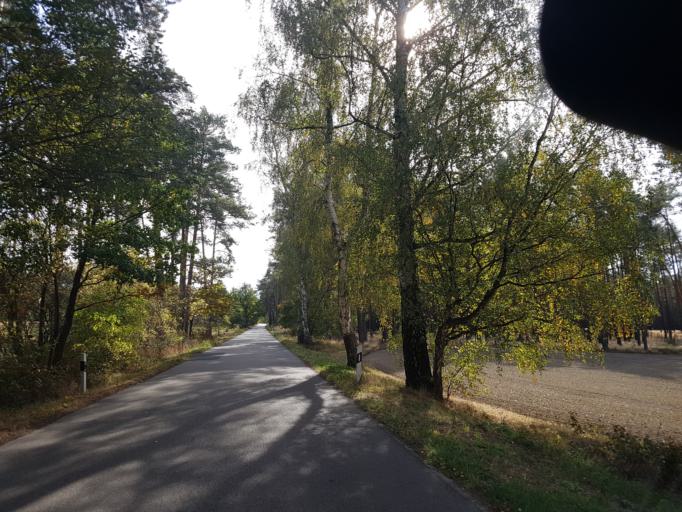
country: DE
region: Brandenburg
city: Schlieben
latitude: 51.7667
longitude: 13.3372
